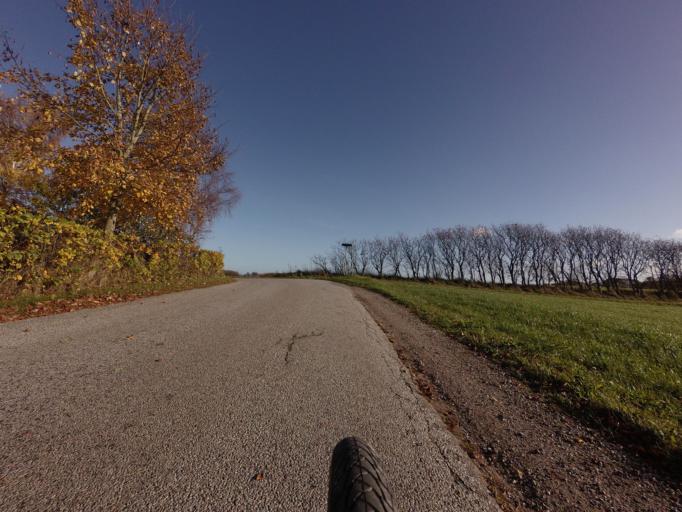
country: DK
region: Central Jutland
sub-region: Syddjurs Kommune
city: Ryomgard
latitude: 56.4569
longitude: 10.6302
